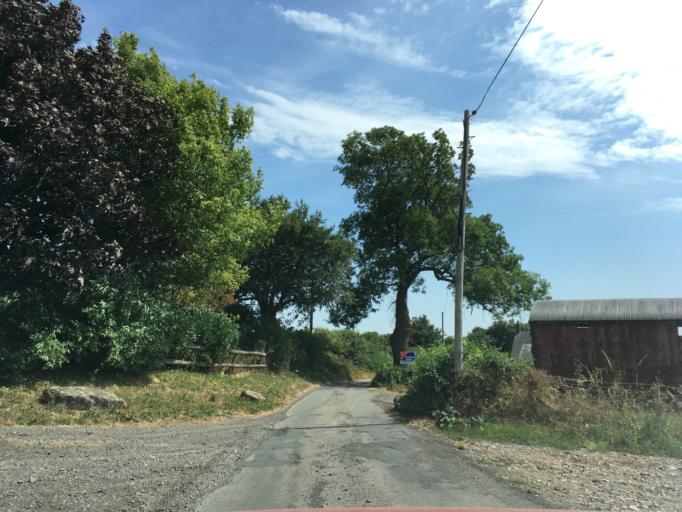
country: GB
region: Wales
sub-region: Monmouthshire
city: Magor
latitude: 51.6071
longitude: -2.8468
